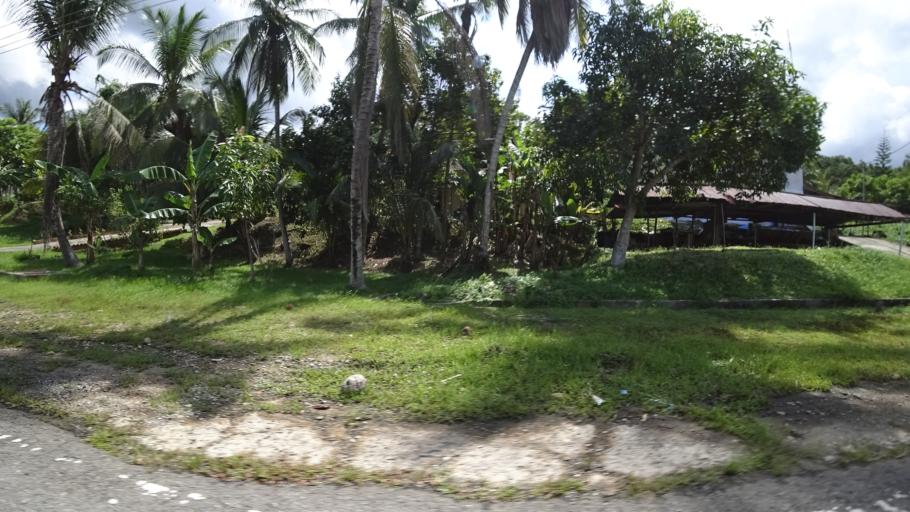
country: BN
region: Brunei and Muara
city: Bandar Seri Begawan
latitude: 4.8794
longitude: 114.9627
